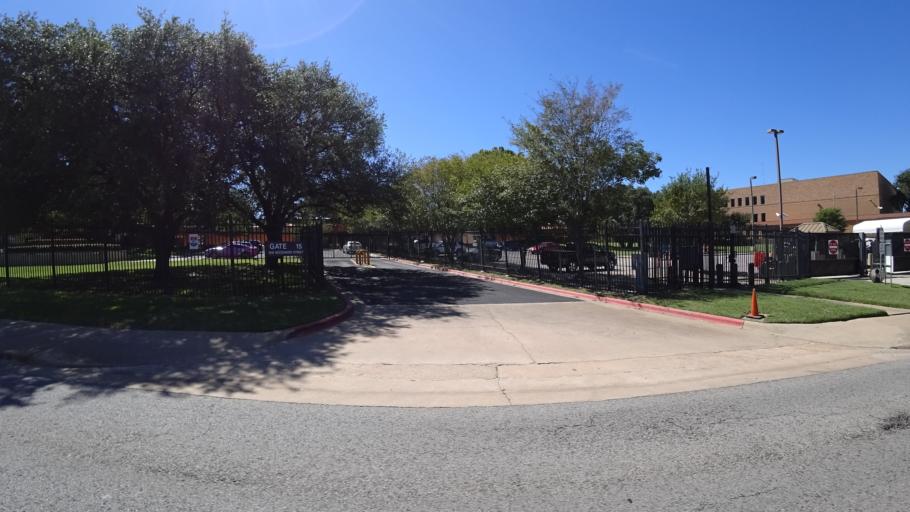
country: US
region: Texas
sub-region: Travis County
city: Austin
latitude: 30.2212
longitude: -97.7453
